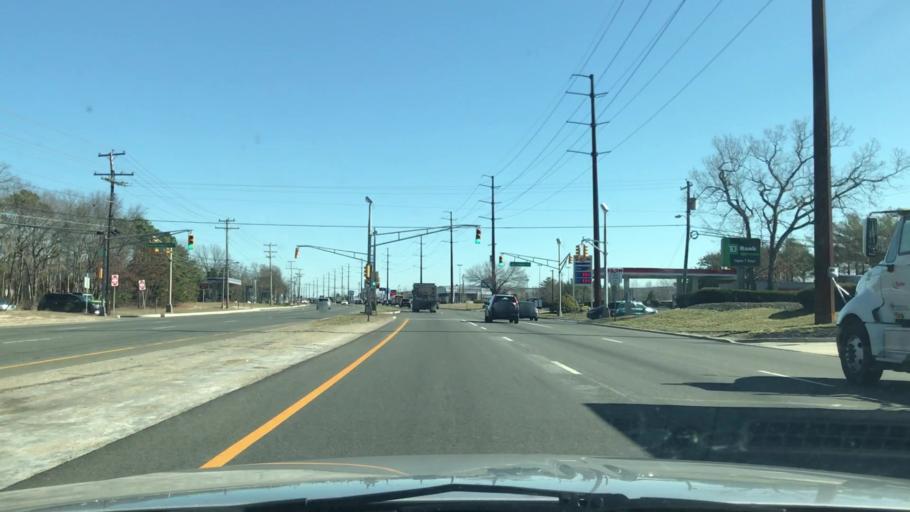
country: US
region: New Jersey
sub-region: Ocean County
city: Manahawkin
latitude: 39.7055
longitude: -74.2748
